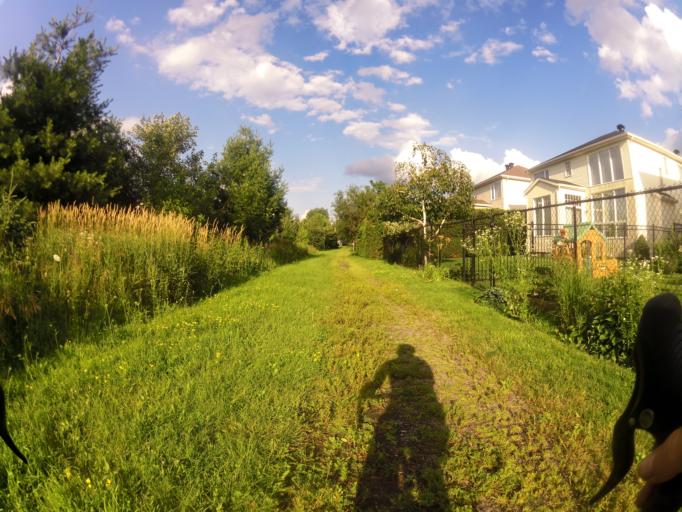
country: CA
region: Ontario
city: Ottawa
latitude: 45.2864
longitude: -75.6898
